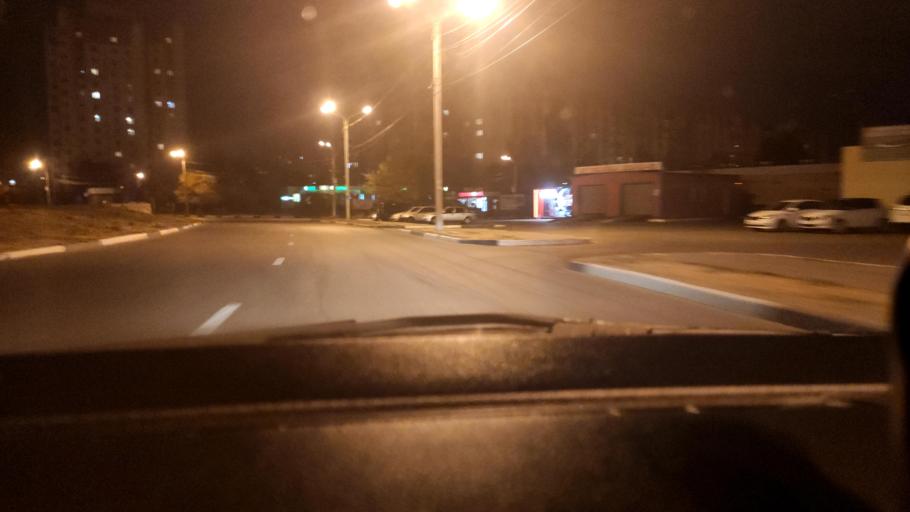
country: RU
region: Voronezj
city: Podgornoye
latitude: 51.7153
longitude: 39.1717
